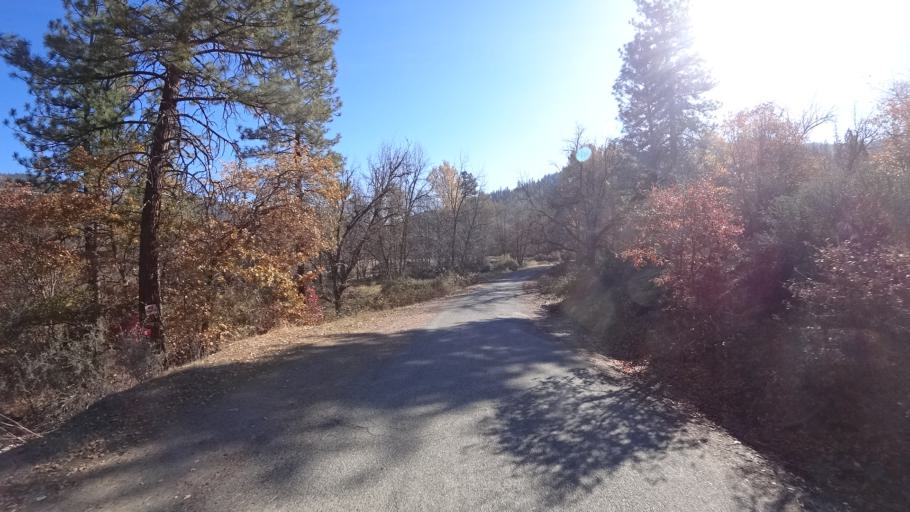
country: US
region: California
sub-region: Siskiyou County
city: Yreka
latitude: 41.8422
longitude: -122.8938
